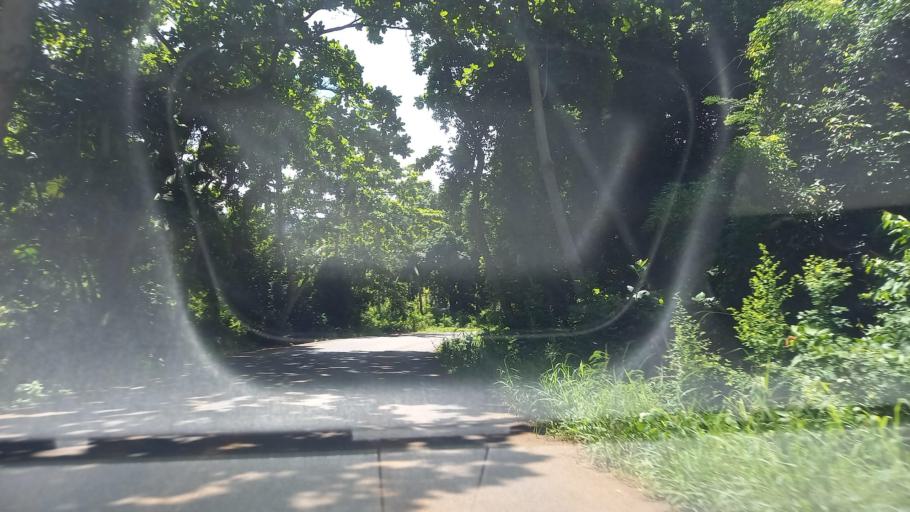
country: YT
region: Ouangani
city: Ouangani
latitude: -12.8787
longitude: 45.1244
